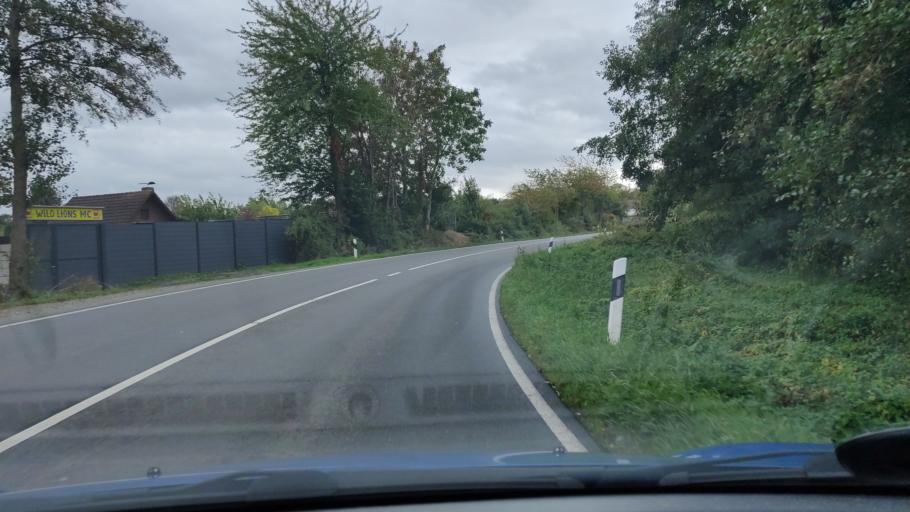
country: DE
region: Lower Saxony
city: Seelze
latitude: 52.3921
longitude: 9.5755
